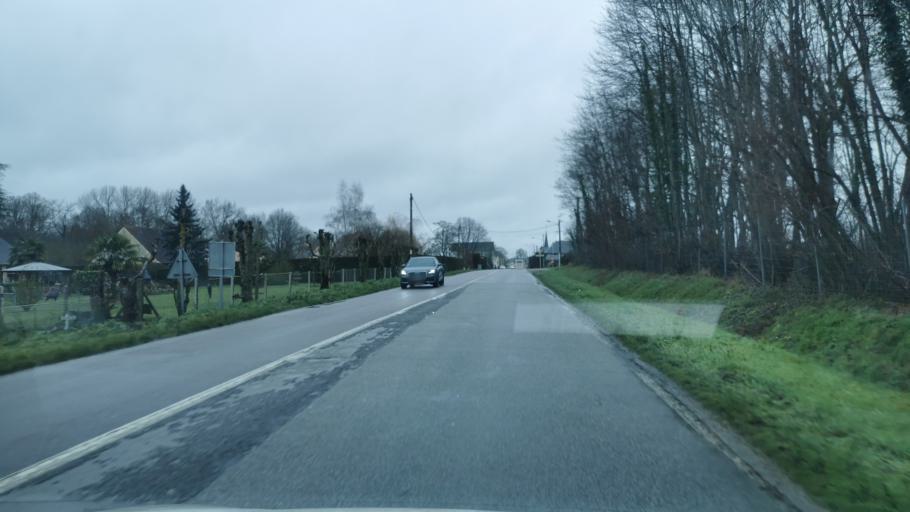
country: FR
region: Haute-Normandie
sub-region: Departement de l'Eure
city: Normanville
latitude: 49.0782
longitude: 1.1792
